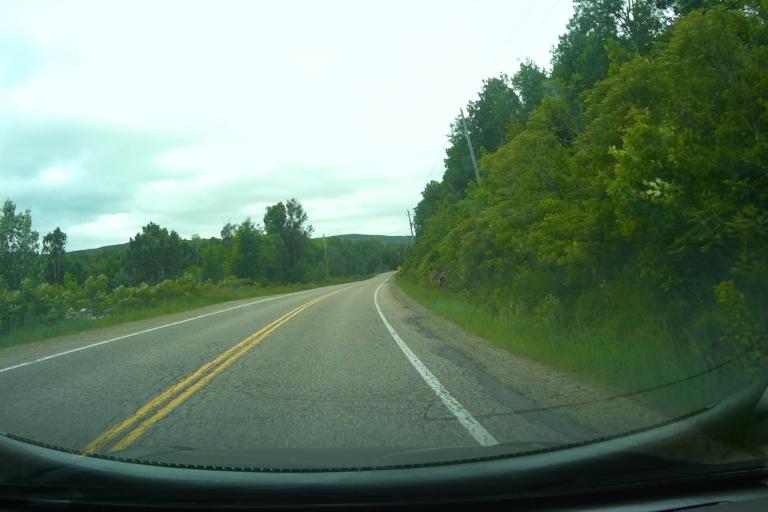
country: CA
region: Ontario
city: Pembroke
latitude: 45.4704
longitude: -77.2181
